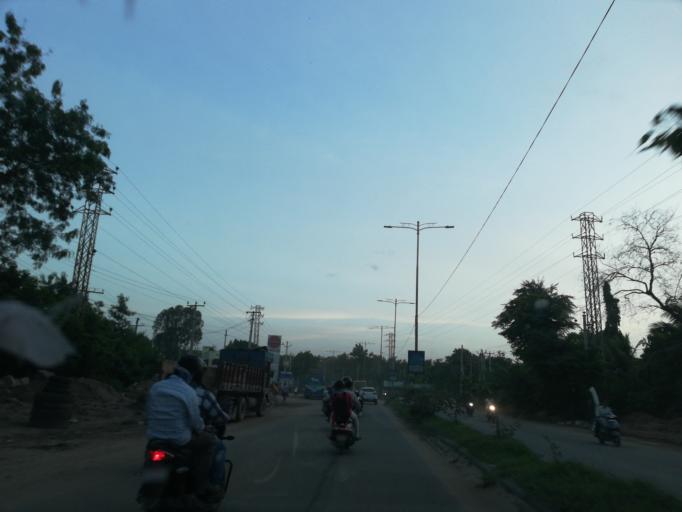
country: IN
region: Telangana
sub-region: Medak
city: Serilingampalle
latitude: 17.5284
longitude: 78.3546
